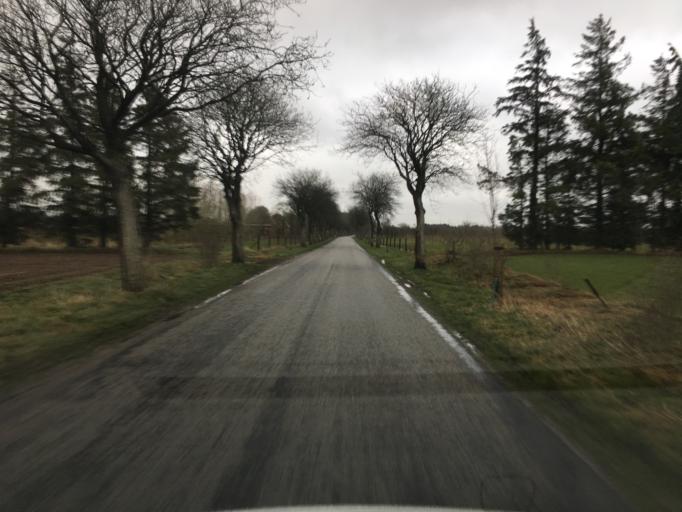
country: DK
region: South Denmark
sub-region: Aabenraa Kommune
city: Tinglev
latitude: 54.9012
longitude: 9.3221
